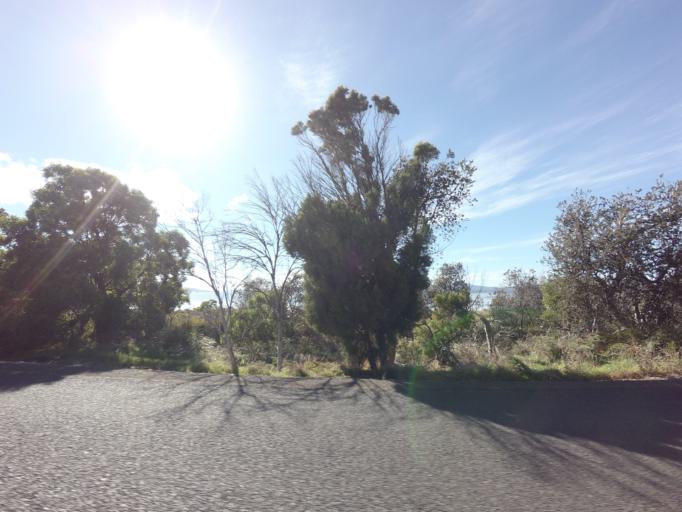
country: AU
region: Tasmania
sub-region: Clarence
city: Sandford
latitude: -43.0079
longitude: 147.7077
